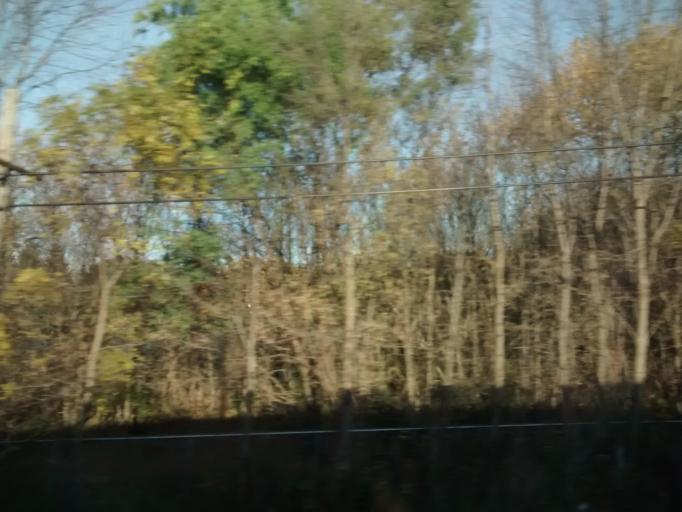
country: CA
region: Ontario
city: Mississauga
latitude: 43.5647
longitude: -79.5777
